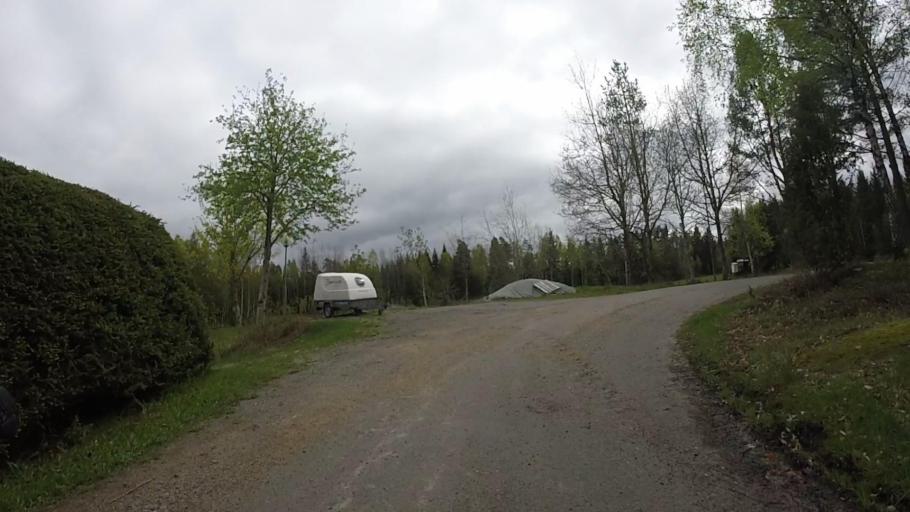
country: SE
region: Vaestra Goetaland
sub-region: Trollhattan
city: Sjuntorp
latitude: 58.2389
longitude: 12.2100
